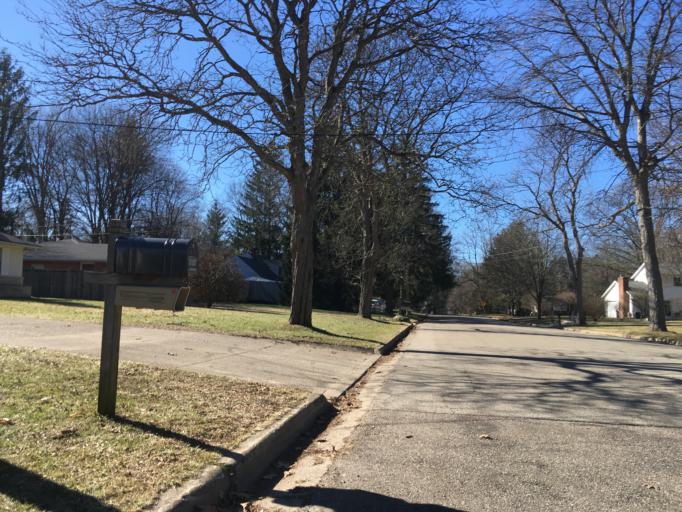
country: US
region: Michigan
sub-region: Kalamazoo County
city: Westwood
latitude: 42.2638
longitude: -85.6248
